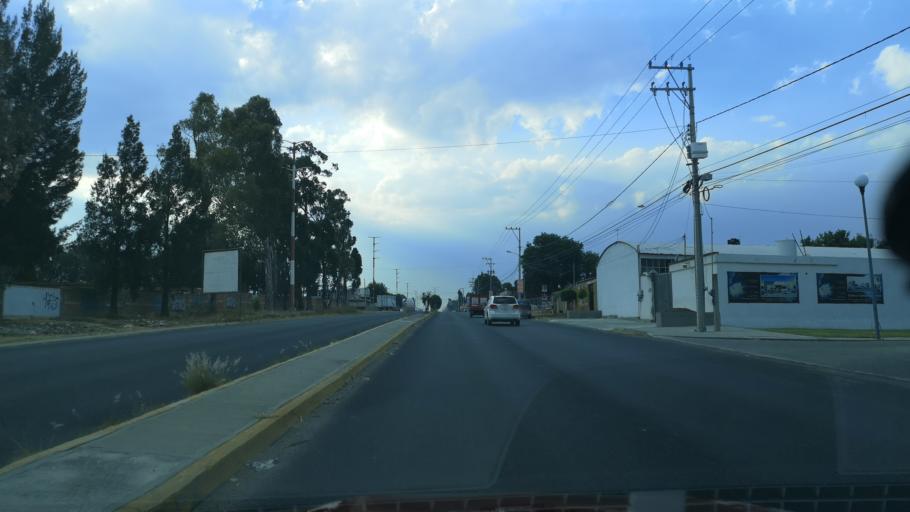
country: MX
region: Puebla
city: Cuanala
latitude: 19.1043
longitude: -98.3486
